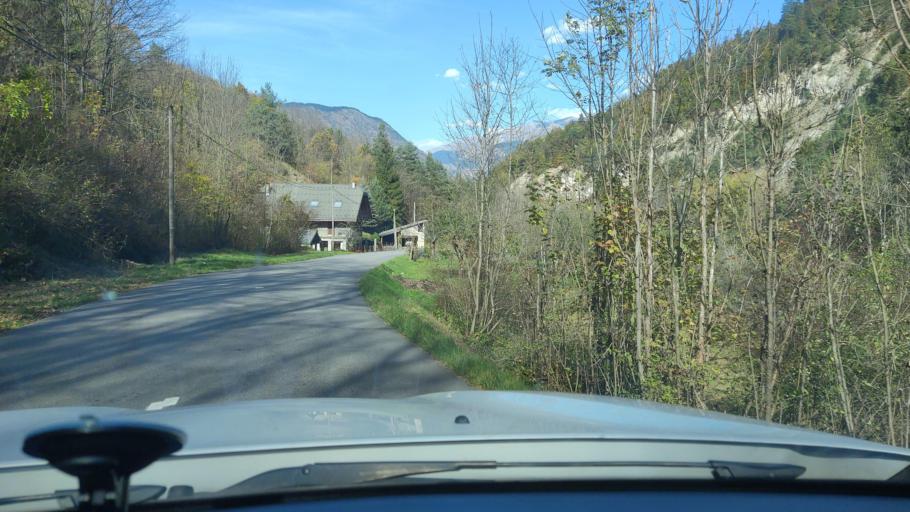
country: FR
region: Rhone-Alpes
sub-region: Departement de la Savoie
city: Saint-Jean-de-Maurienne
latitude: 45.2434
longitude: 6.3205
